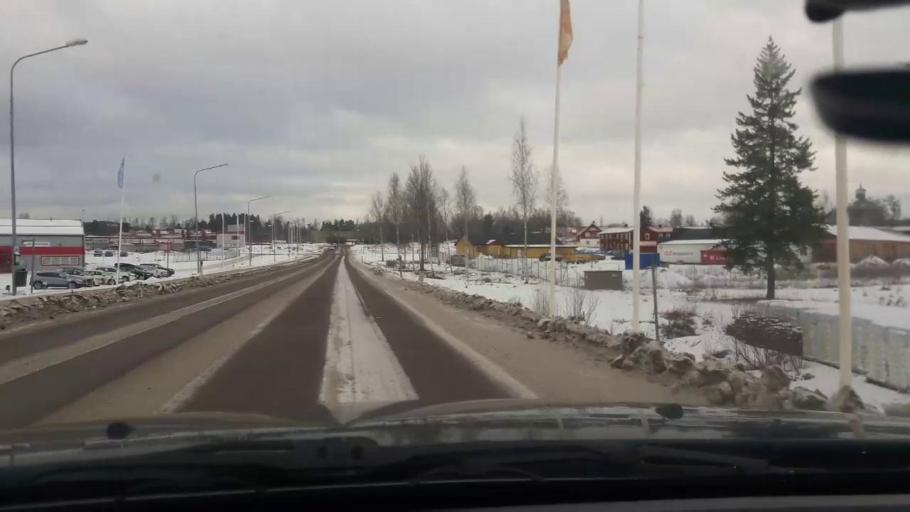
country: SE
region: Gaevleborg
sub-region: Bollnas Kommun
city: Bollnas
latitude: 61.3410
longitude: 16.3866
